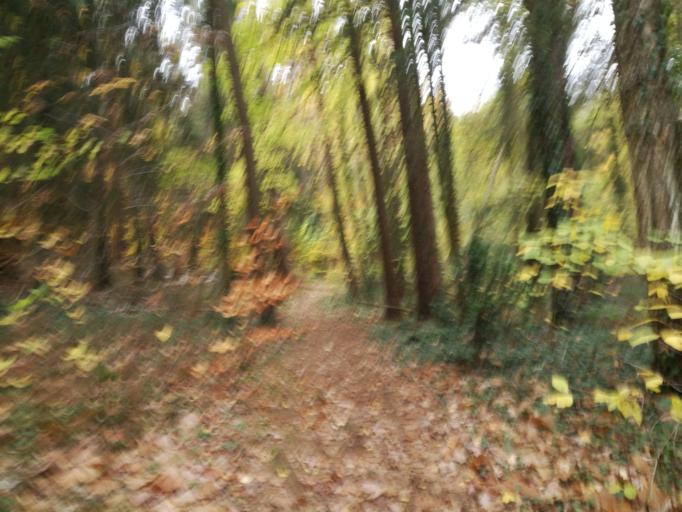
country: DE
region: Bavaria
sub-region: Regierungsbezirk Mittelfranken
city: Zirndorf
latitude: 49.4687
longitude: 10.9364
